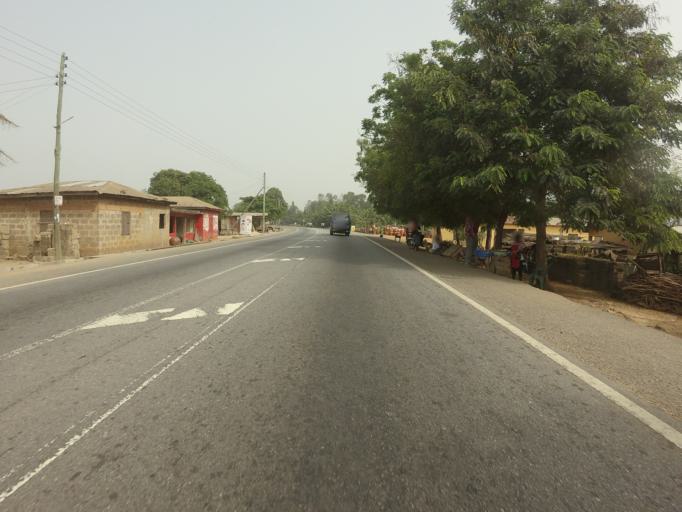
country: GH
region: Volta
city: Anloga
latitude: 6.0081
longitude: 0.5502
